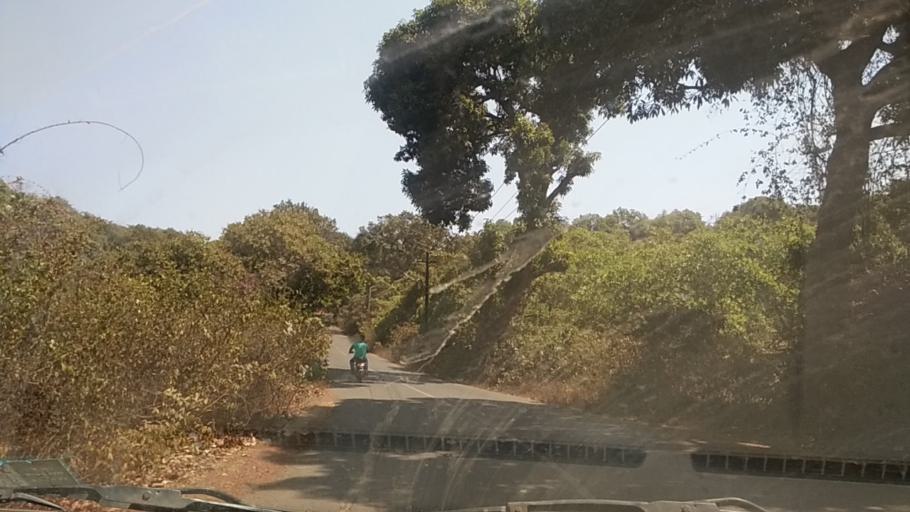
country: IN
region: Goa
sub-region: North Goa
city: Dicholi
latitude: 15.5820
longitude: 73.9350
